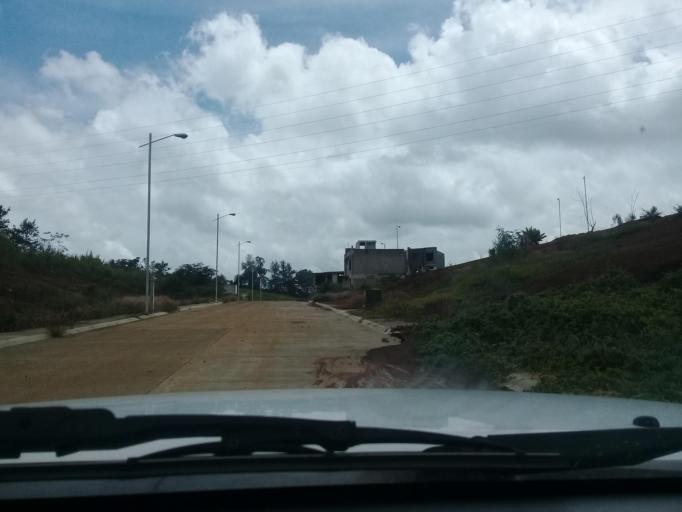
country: MX
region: Veracruz
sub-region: Xalapa
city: Lomas Verdes
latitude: 19.4998
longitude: -96.9129
